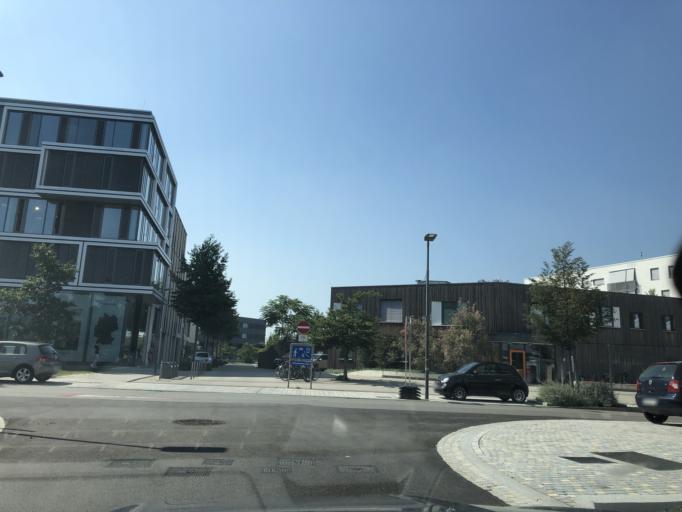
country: DE
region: Baden-Wuerttemberg
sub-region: Karlsruhe Region
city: Heidelberg
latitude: 49.3993
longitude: 8.6721
